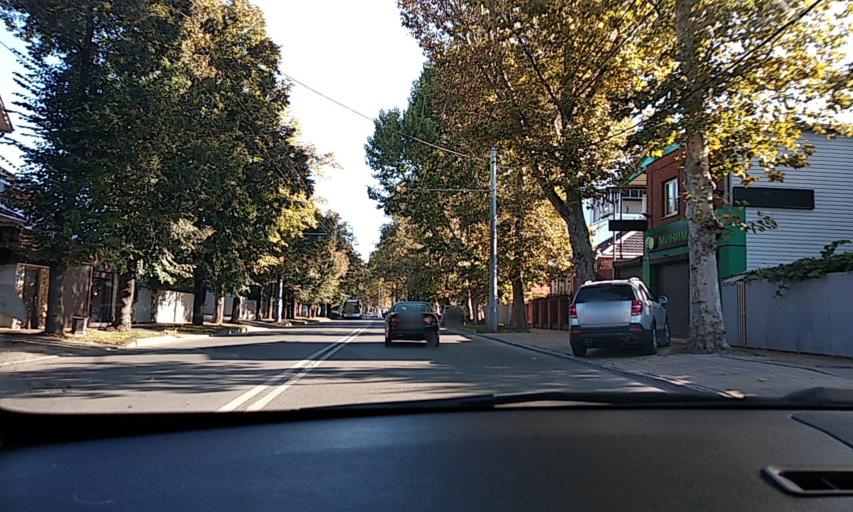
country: RU
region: Krasnodarskiy
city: Pashkovskiy
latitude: 45.0206
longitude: 39.1059
